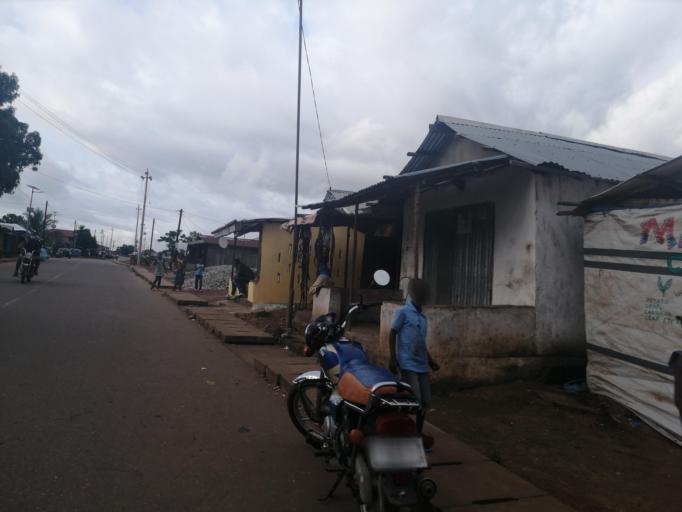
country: SL
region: Northern Province
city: Port Loko
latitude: 8.7723
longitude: -12.7888
